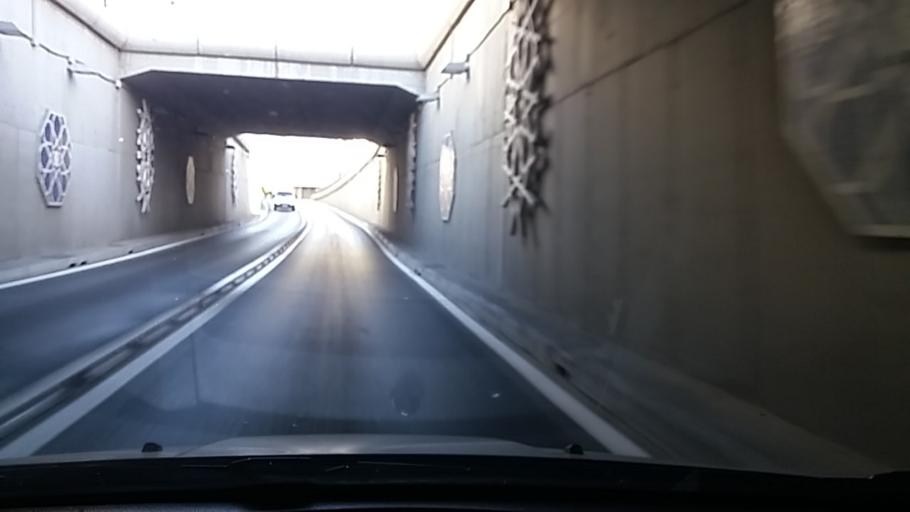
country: MA
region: Tanger-Tetouan
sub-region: Tanger-Assilah
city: Tangier
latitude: 35.7720
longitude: -5.8145
